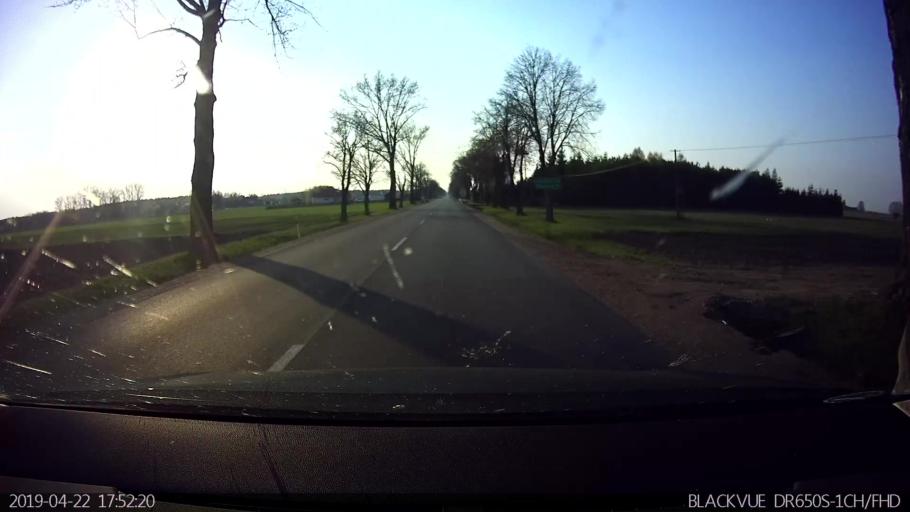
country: PL
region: Masovian Voivodeship
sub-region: Powiat wegrowski
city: Wegrow
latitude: 52.4419
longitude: 21.9787
